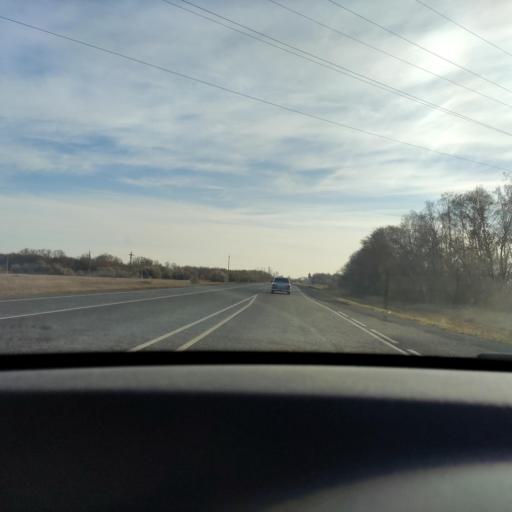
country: RU
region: Samara
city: Krasnoarmeyskoye
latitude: 52.7738
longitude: 50.0233
